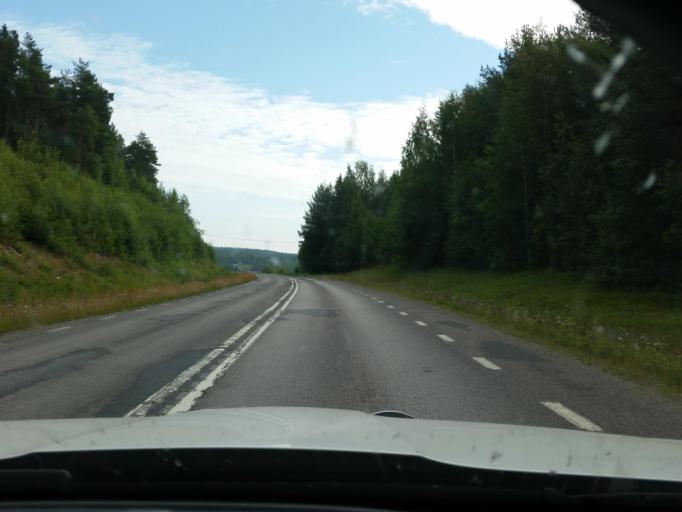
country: SE
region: Norrbotten
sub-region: Alvsbyns Kommun
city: AElvsbyn
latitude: 65.6771
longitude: 20.7696
